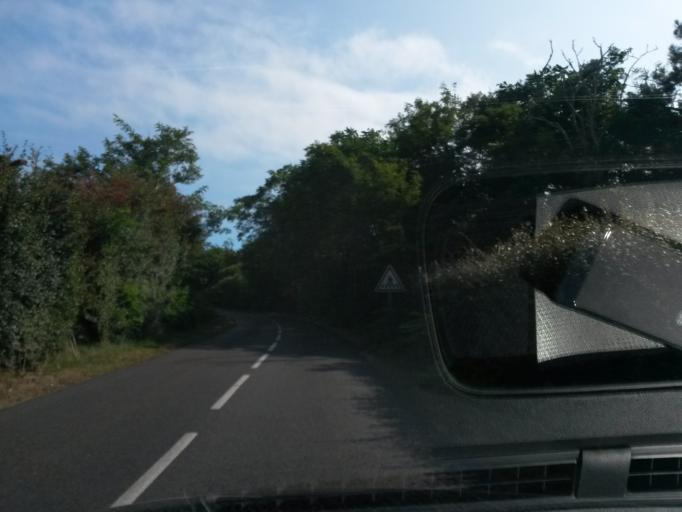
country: FR
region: Pays de la Loire
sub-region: Departement de la Vendee
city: Les Sables-d'Olonne
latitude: 46.5251
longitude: -1.8105
